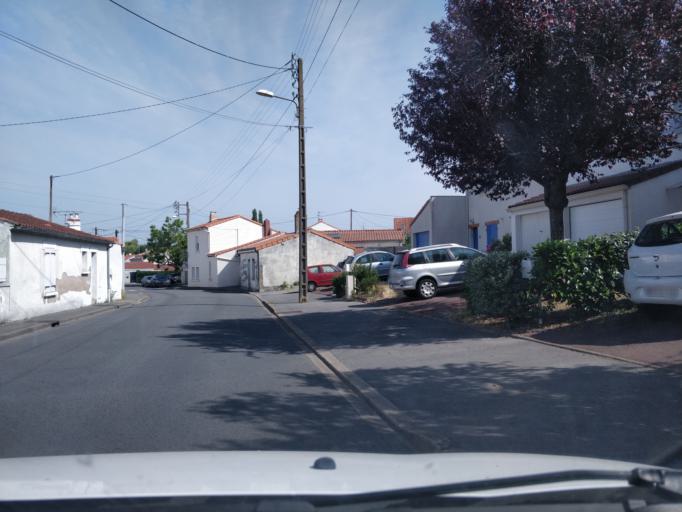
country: FR
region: Pays de la Loire
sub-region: Departement de la Loire-Atlantique
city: Saint-Sebastien-sur-Loire
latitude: 47.2007
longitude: -1.4932
